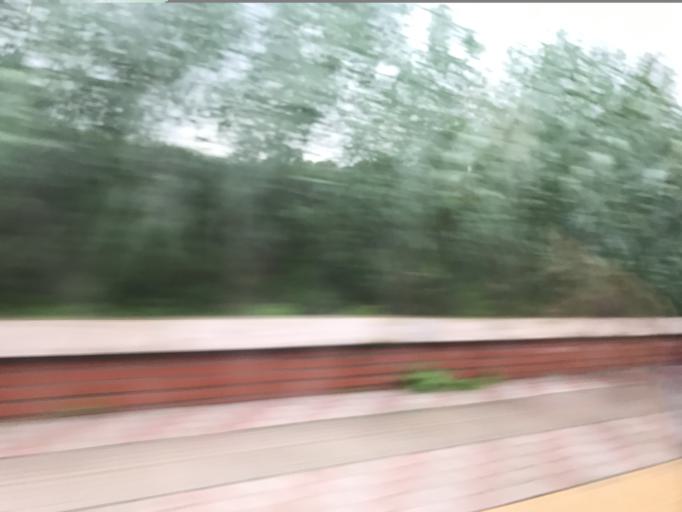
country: VA
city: Vatican City
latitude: 41.8479
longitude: 12.4551
